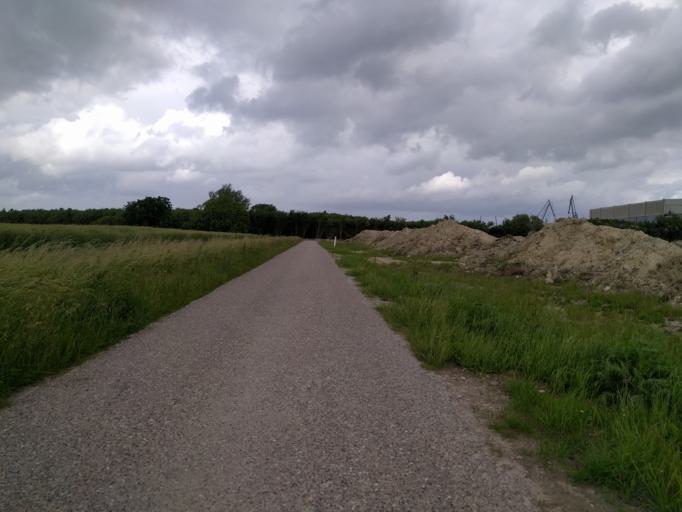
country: DK
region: South Denmark
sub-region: Kerteminde Kommune
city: Munkebo
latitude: 55.4619
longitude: 10.5168
